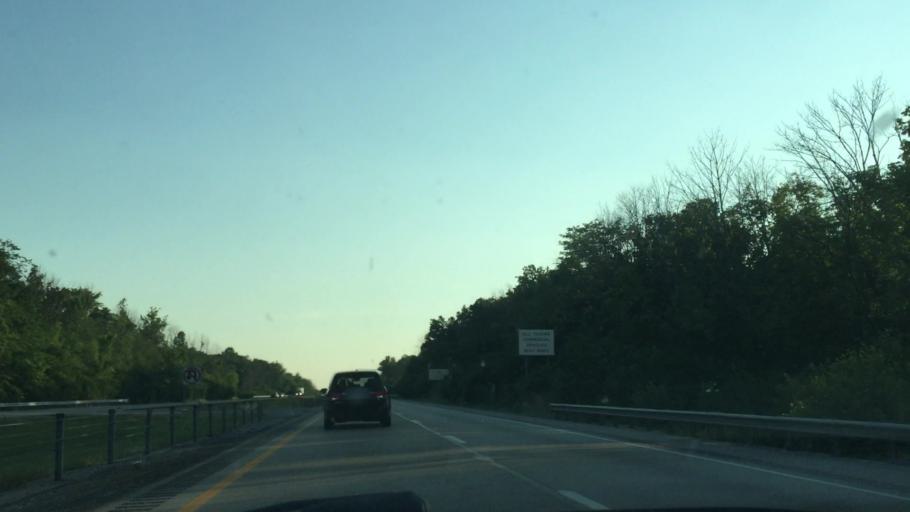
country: US
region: Kentucky
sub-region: Boone County
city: Walton
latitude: 38.8713
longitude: -84.6349
